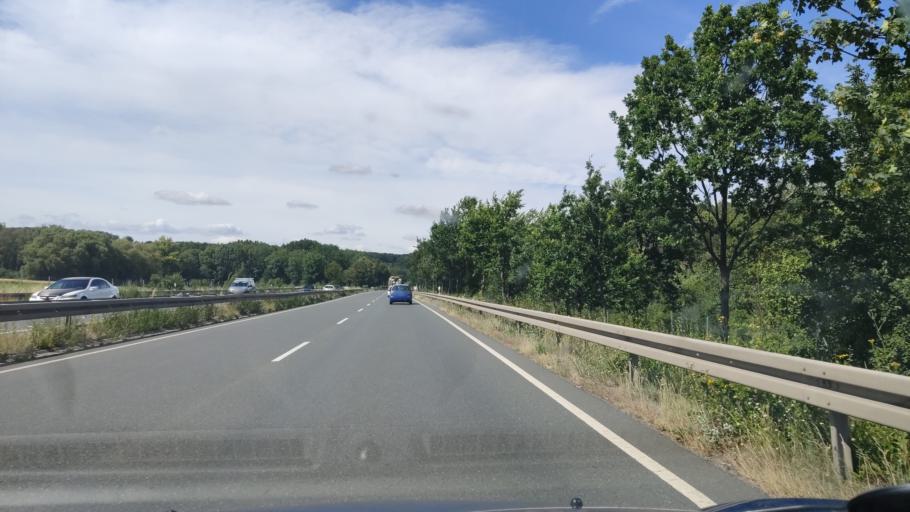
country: DE
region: Lower Saxony
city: Ronnenberg
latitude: 52.3406
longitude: 9.6435
